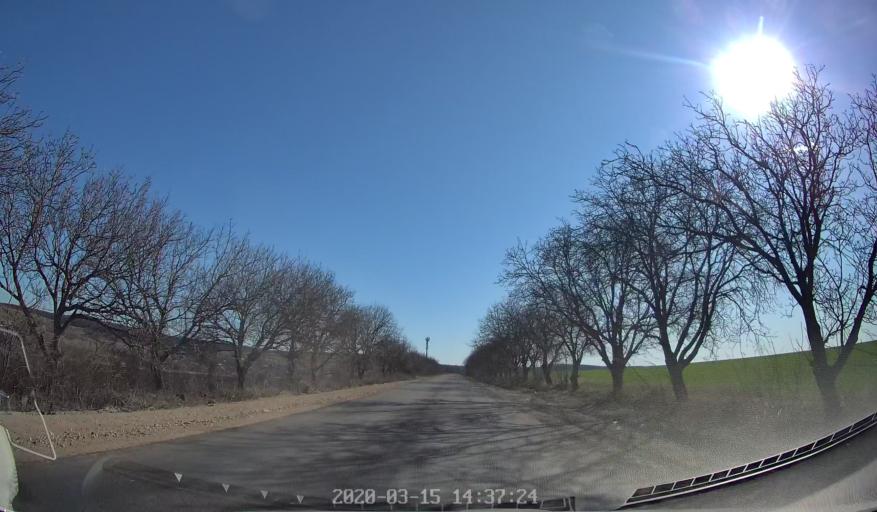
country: MD
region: Orhei
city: Orhei
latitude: 47.3160
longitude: 28.9250
